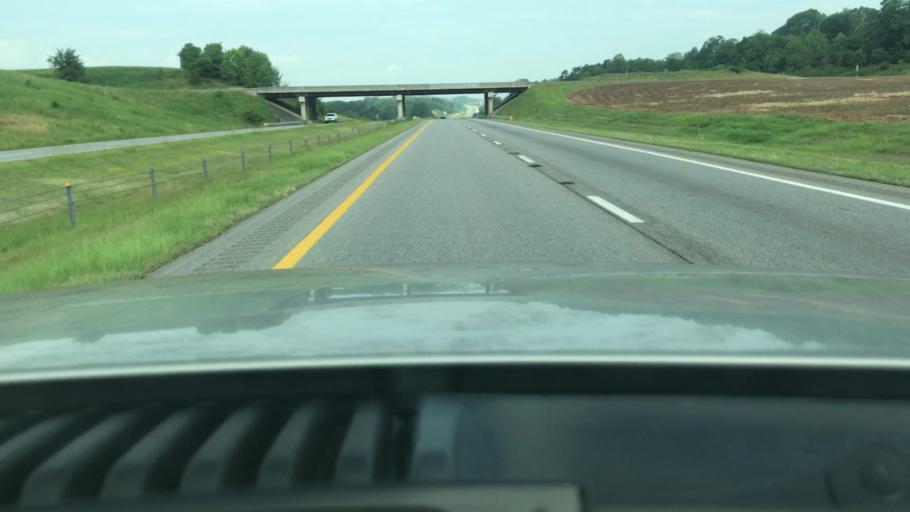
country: US
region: North Carolina
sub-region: Yadkin County
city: Jonesville
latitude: 36.1300
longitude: -80.8403
